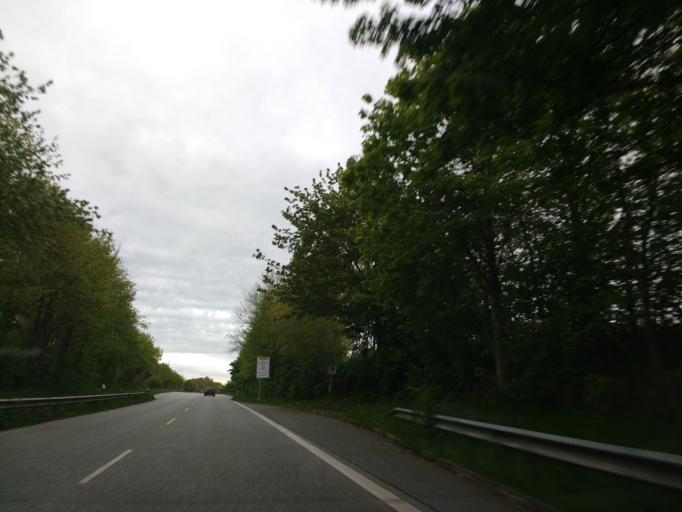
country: DE
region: Schleswig-Holstein
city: Damp
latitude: 54.5782
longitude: 9.9575
